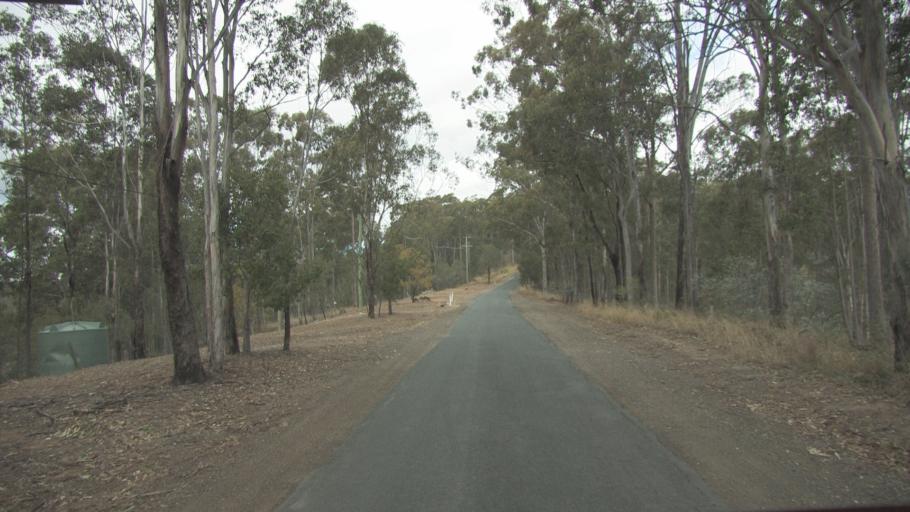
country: AU
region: Queensland
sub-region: Logan
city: Cedar Vale
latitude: -27.8928
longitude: 153.0327
